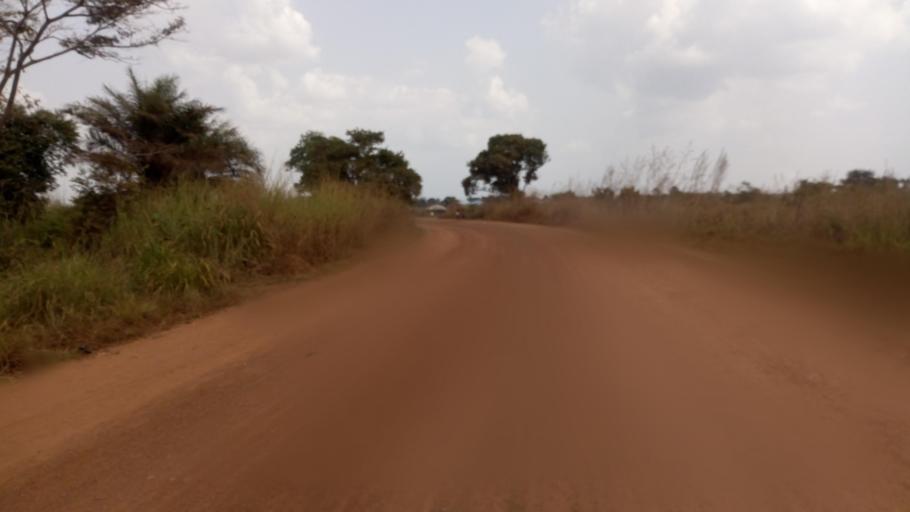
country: SL
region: Southern Province
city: Mogbwemo
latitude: 7.7862
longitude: -12.3123
